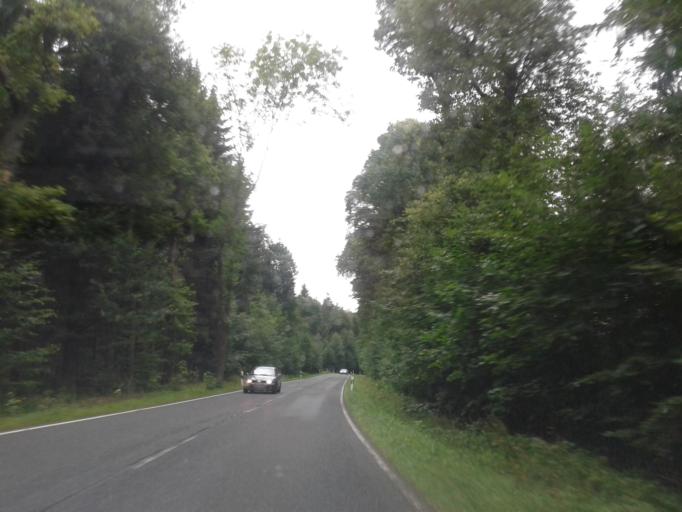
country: DE
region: Saxony
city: Niederschona
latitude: 50.9480
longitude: 13.4877
